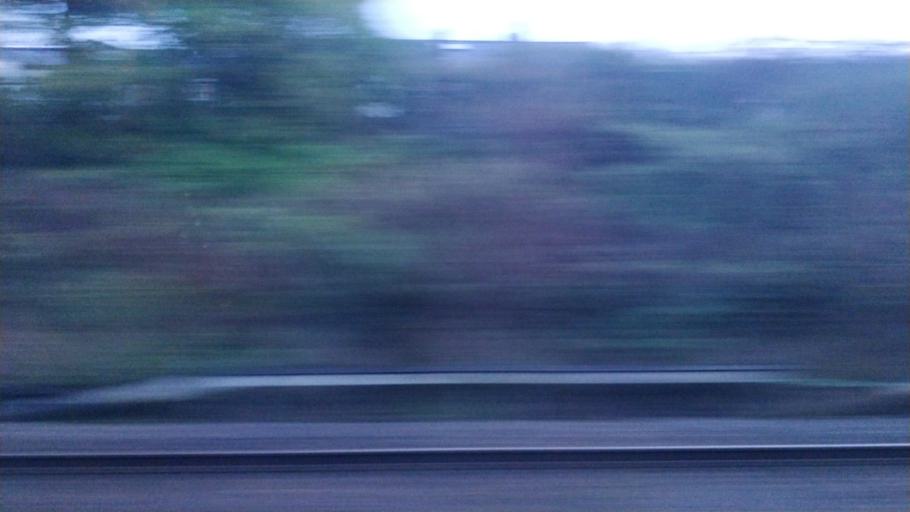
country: GB
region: England
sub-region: Borough of Wigan
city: Hindley
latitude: 53.5435
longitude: -2.5550
